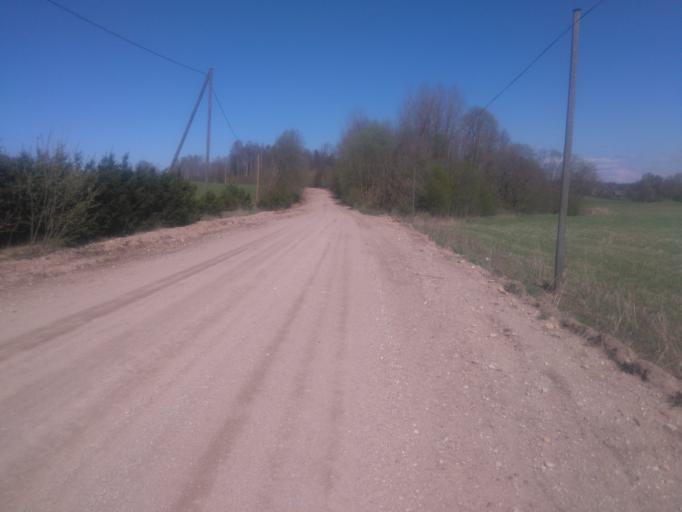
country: LV
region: Vecpiebalga
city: Vecpiebalga
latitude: 57.0233
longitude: 25.8373
